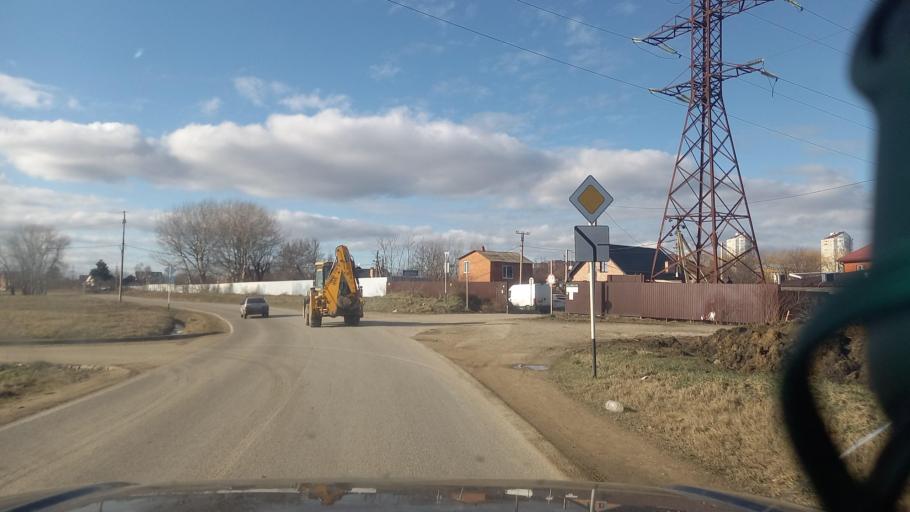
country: RU
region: Adygeya
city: Yablonovskiy
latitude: 45.0175
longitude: 38.9109
